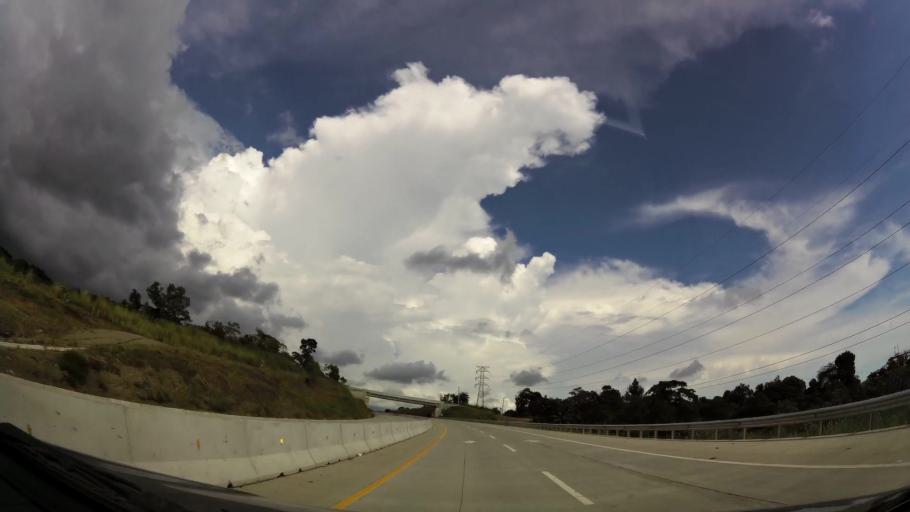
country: PA
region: Panama
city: Tocumen
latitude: 9.0916
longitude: -79.4266
